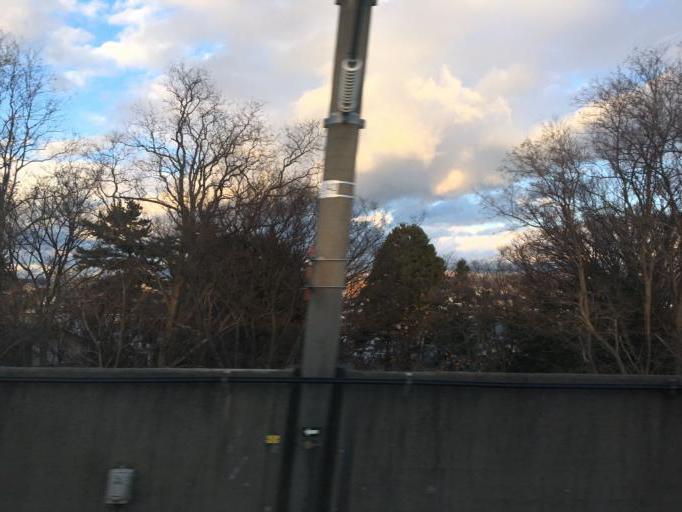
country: JP
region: Iwate
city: Morioka-shi
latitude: 39.7120
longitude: 141.1248
